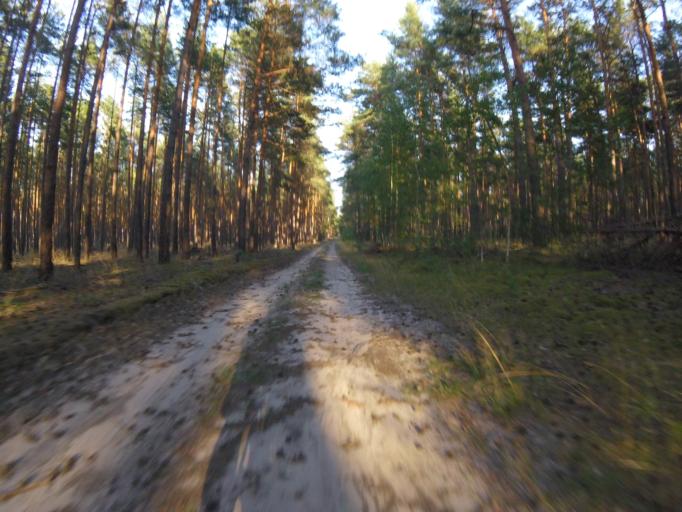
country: DE
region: Brandenburg
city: Schwerin
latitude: 52.1578
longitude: 13.6001
